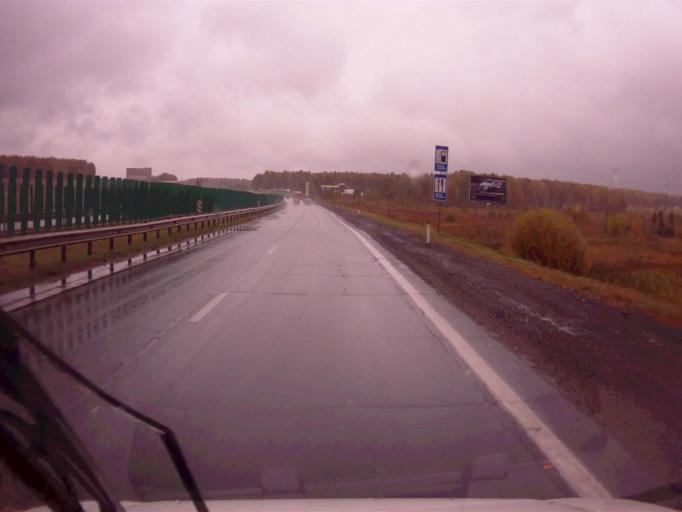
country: RU
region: Chelyabinsk
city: Dolgoderevenskoye
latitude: 55.3223
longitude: 61.3329
